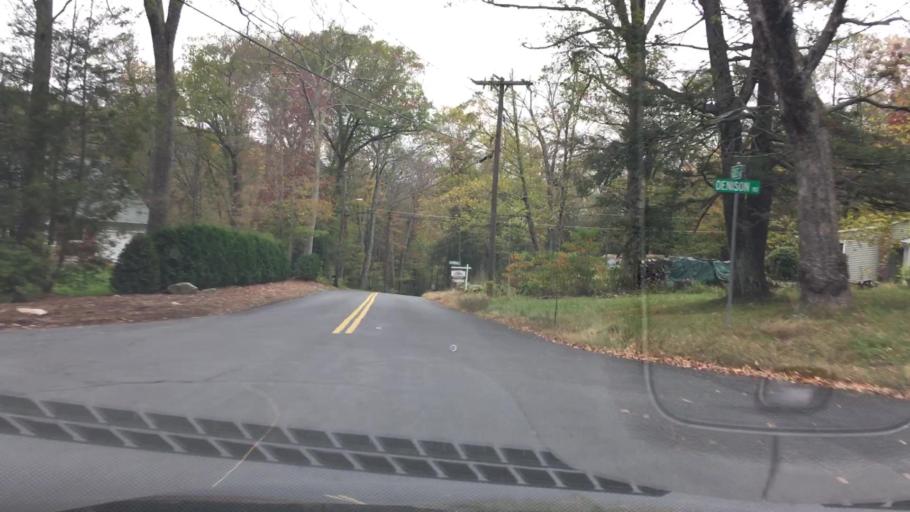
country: US
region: Connecticut
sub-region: Tolland County
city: Somers
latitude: 41.9721
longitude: -72.4156
